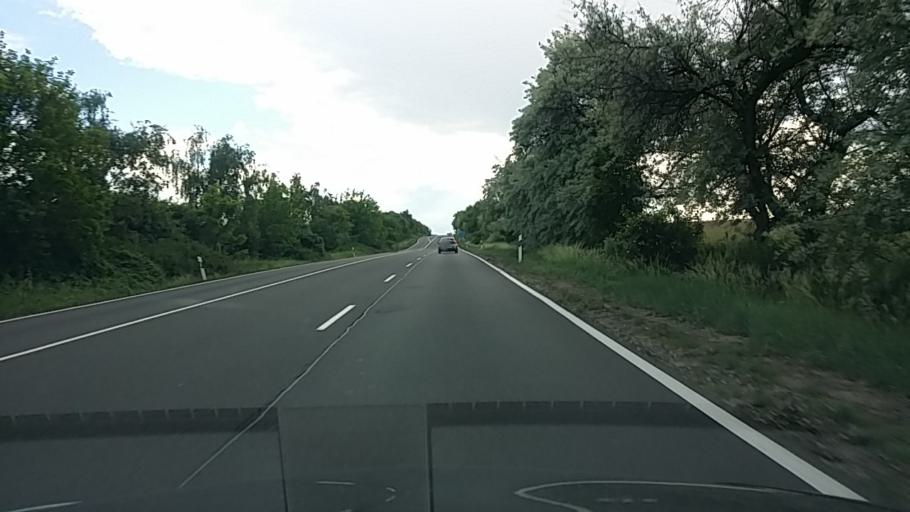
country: HU
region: Nograd
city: Retsag
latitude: 47.9160
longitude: 19.1153
